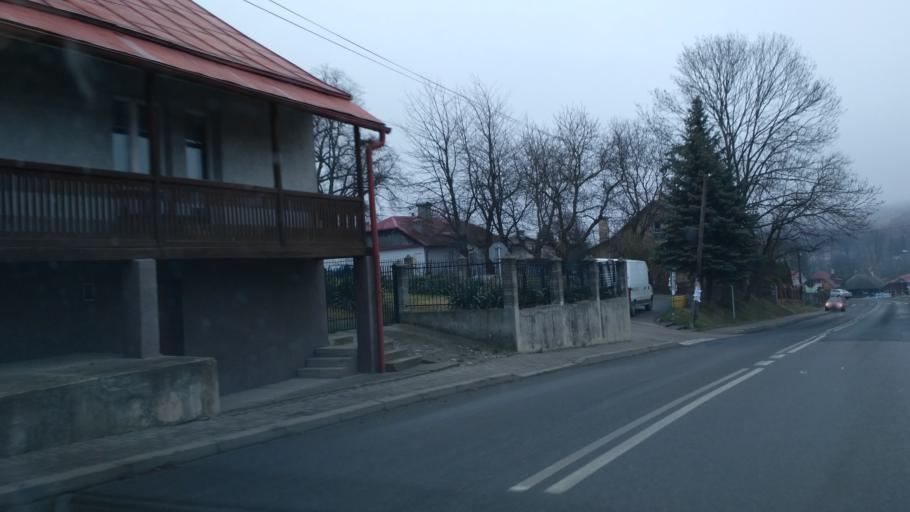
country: PL
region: Subcarpathian Voivodeship
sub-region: Powiat jaroslawski
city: Pruchnik
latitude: 49.9071
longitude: 22.5144
